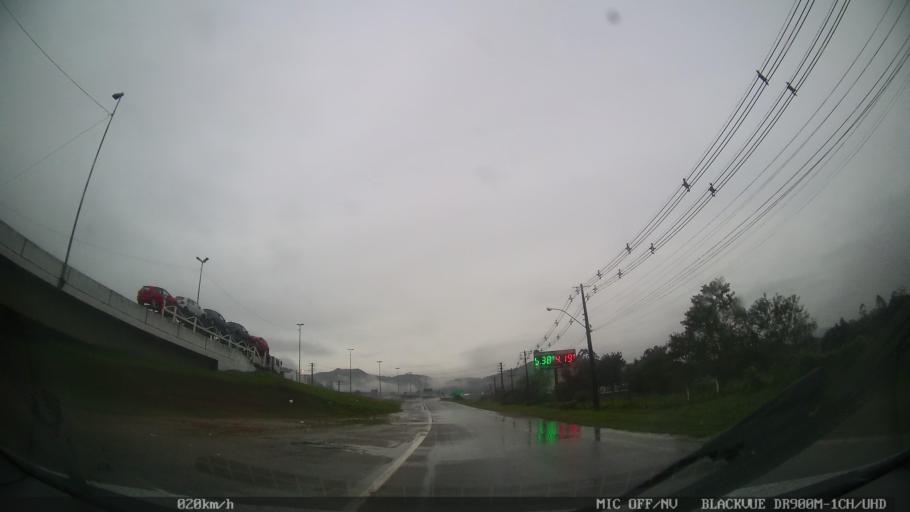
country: BR
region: Santa Catarina
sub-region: Itajai
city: Itajai
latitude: -26.9387
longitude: -48.6969
